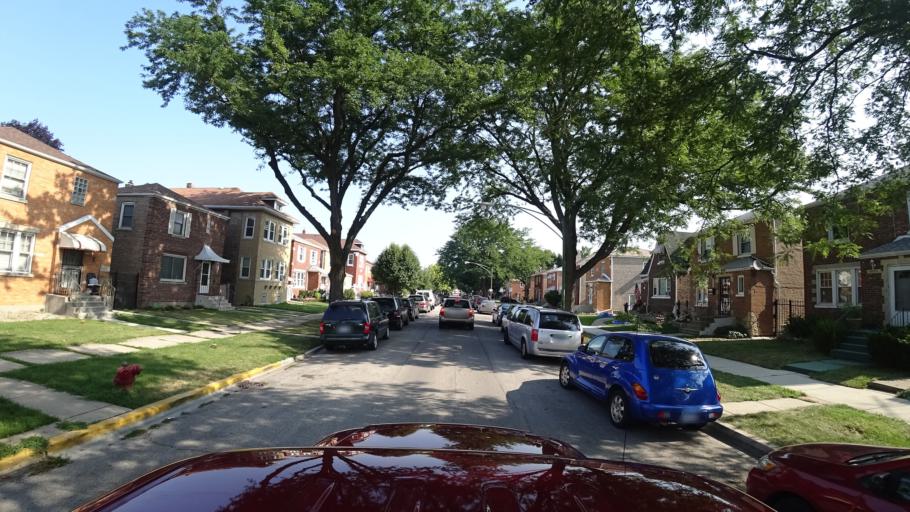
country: US
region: Illinois
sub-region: Cook County
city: Cicero
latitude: 41.8127
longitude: -87.7078
